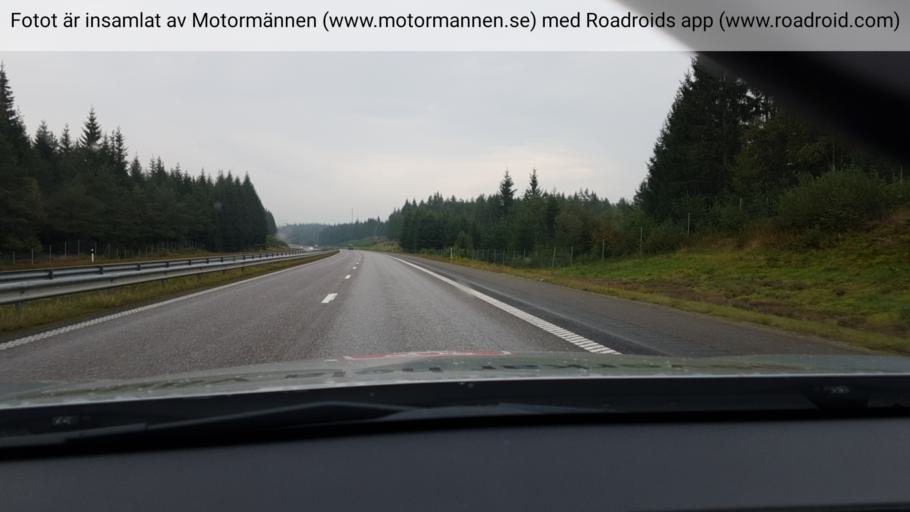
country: SE
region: Vaestra Goetaland
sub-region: Harryda Kommun
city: Hindas
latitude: 57.6684
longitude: 12.3864
